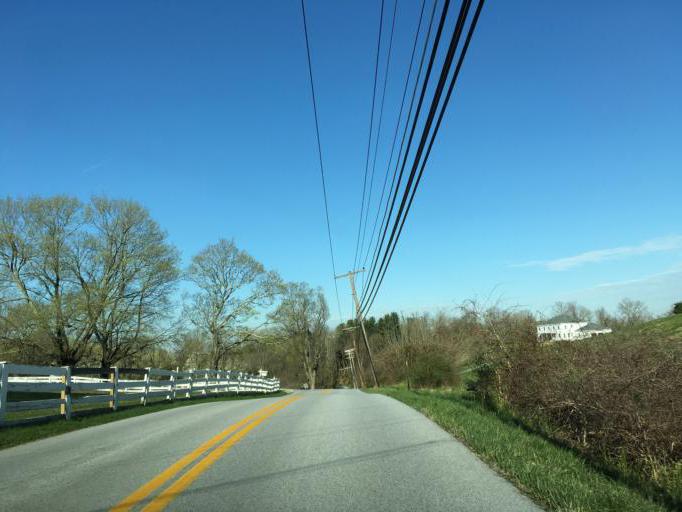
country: US
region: Maryland
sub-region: Baltimore County
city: Hunt Valley
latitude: 39.5429
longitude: -76.6270
